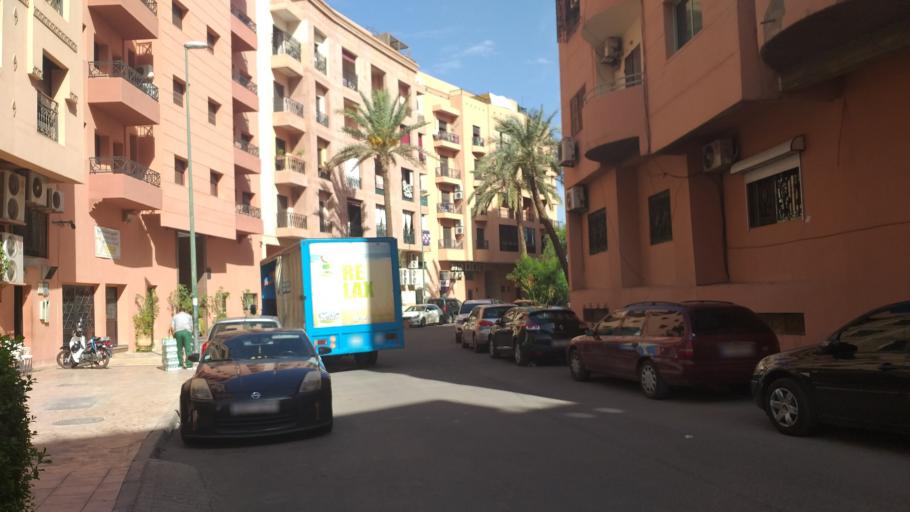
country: MA
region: Marrakech-Tensift-Al Haouz
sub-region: Marrakech
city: Marrakesh
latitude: 31.6541
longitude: -8.0181
